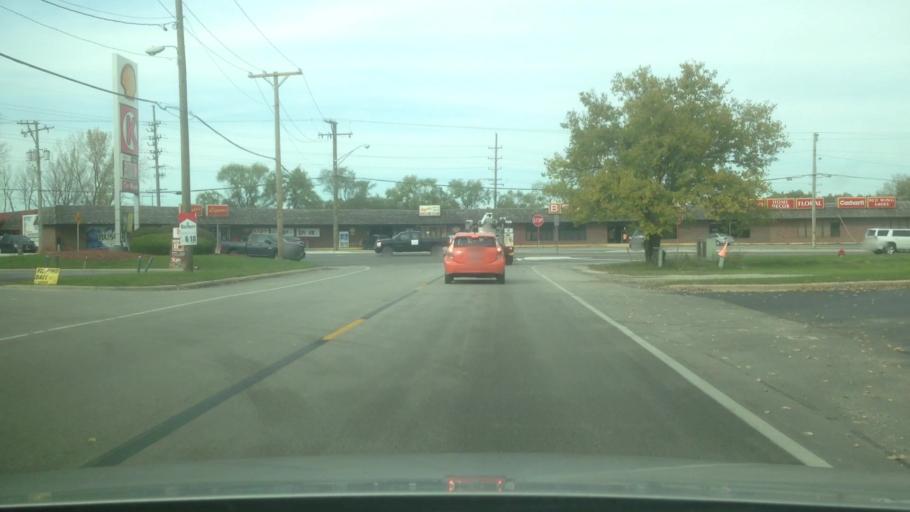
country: US
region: Illinois
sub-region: Will County
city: Wilmington
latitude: 41.3045
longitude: -88.1590
